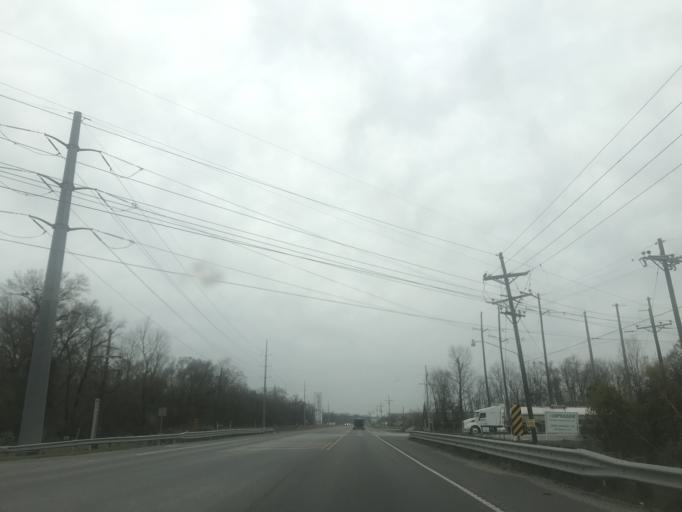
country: US
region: Louisiana
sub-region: Ascension Parish
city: Gonzales
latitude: 30.2104
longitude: -90.9806
